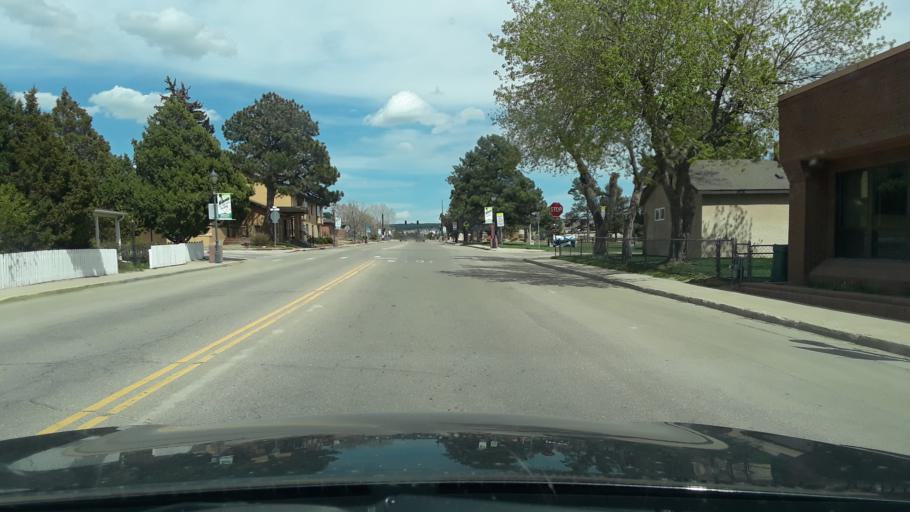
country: US
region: Colorado
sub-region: El Paso County
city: Monument
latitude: 39.0915
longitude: -104.8718
